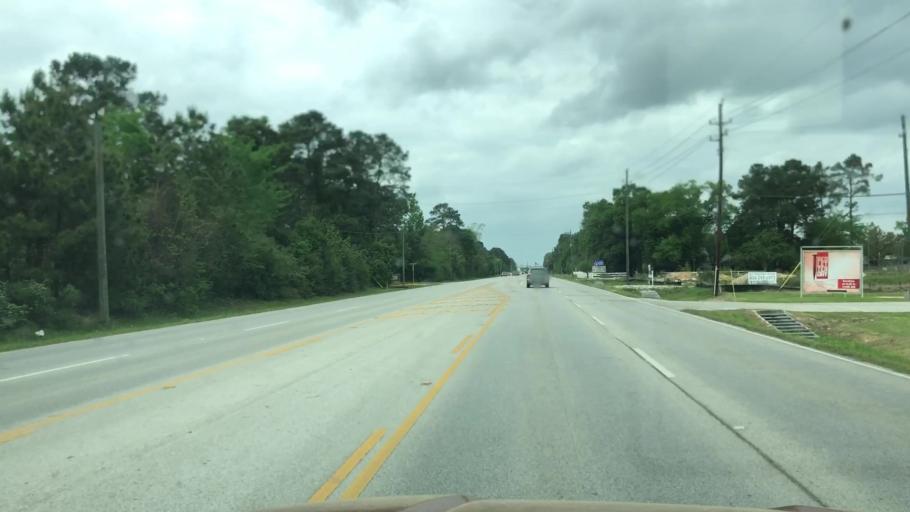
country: US
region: Texas
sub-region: Harris County
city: Spring
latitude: 30.0628
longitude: -95.5005
